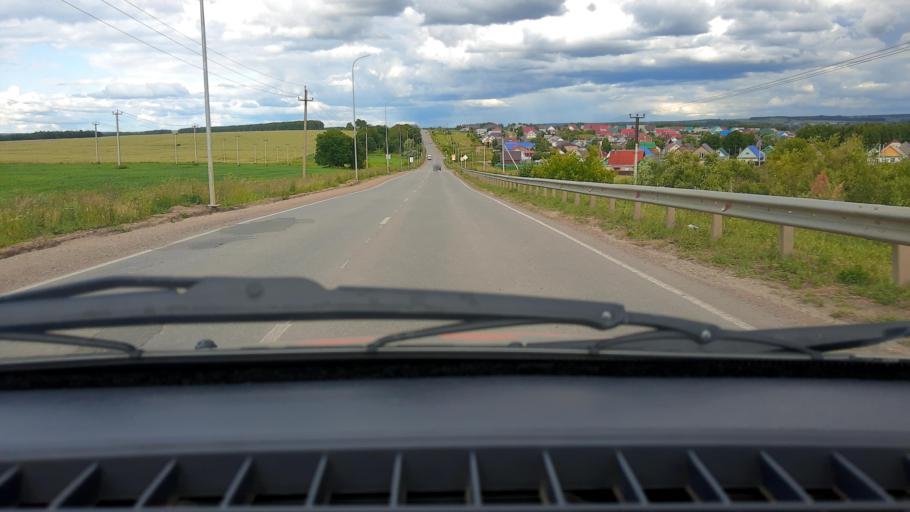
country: RU
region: Bashkortostan
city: Iglino
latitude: 54.8544
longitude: 56.4363
